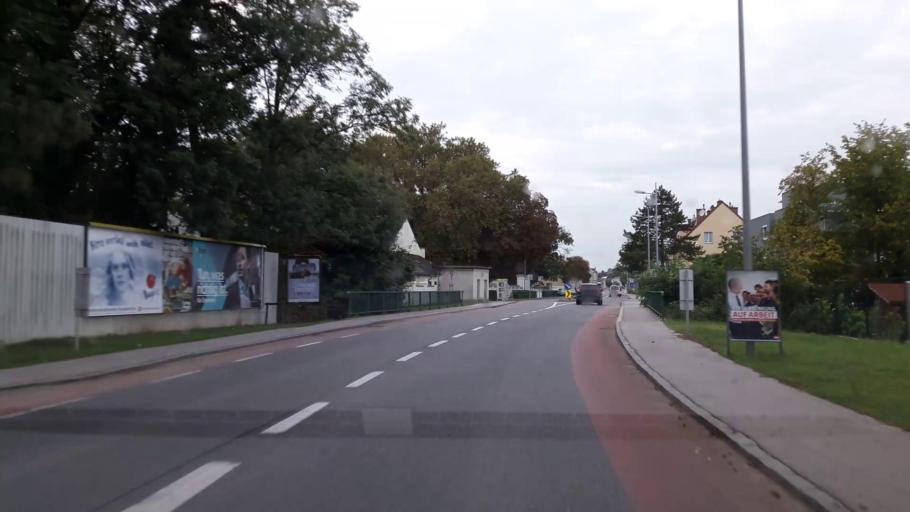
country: AT
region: Lower Austria
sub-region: Politischer Bezirk Wien-Umgebung
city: Schwadorf
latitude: 48.0691
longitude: 16.5870
